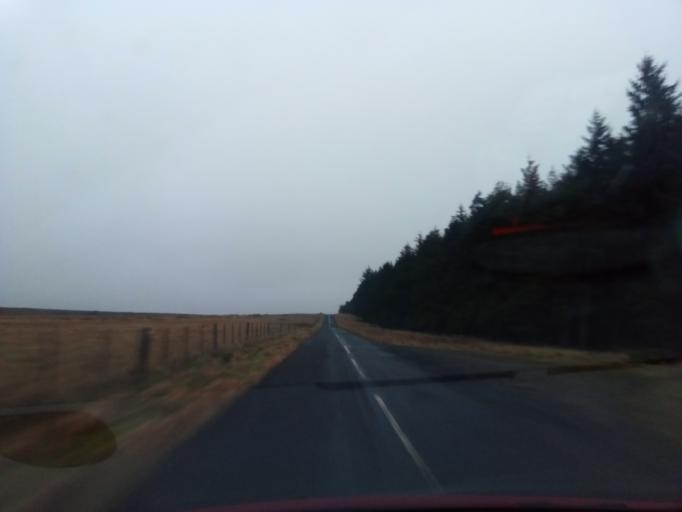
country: GB
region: England
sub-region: Northumberland
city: Otterburn
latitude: 55.2101
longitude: -2.0513
